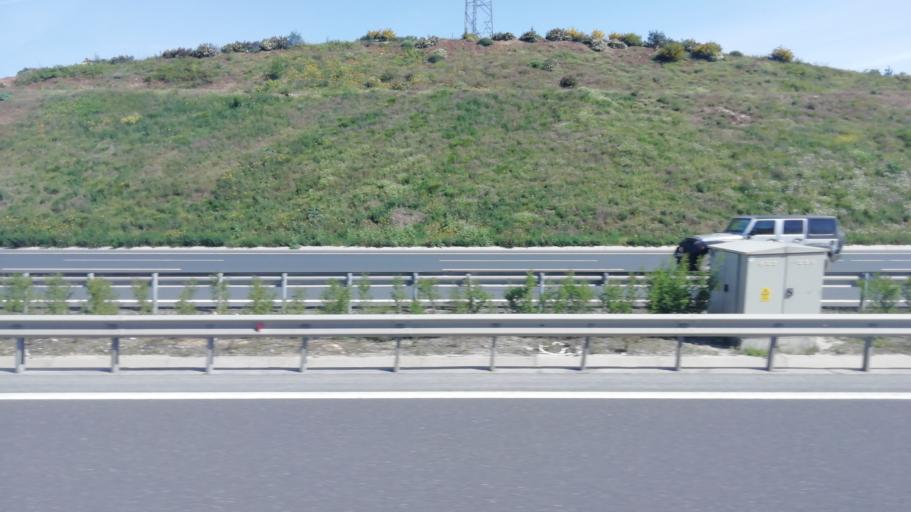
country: TR
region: Istanbul
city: Arikoey
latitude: 41.2207
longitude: 29.0015
